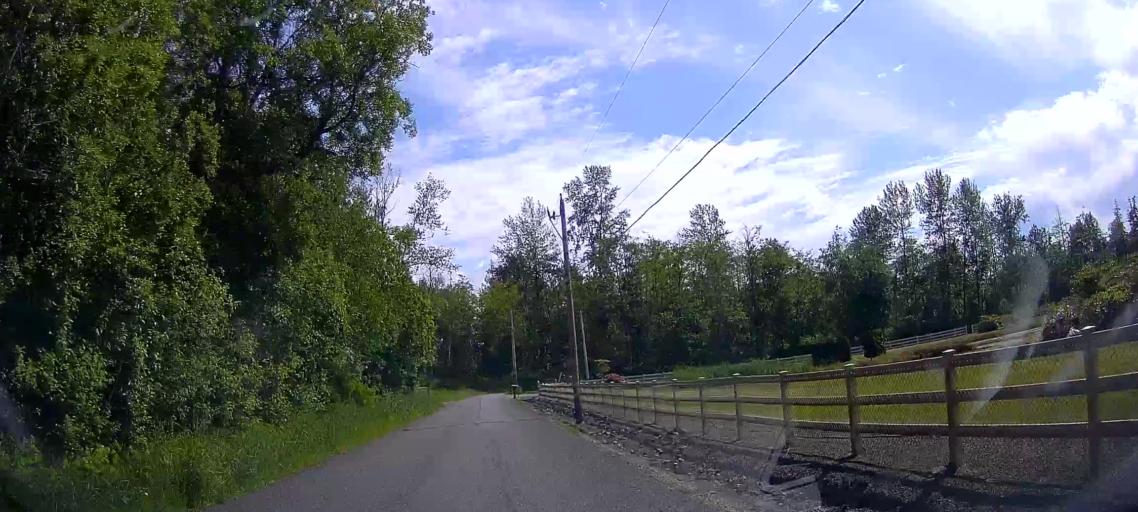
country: US
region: Washington
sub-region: Skagit County
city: Burlington
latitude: 48.5342
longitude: -122.3622
